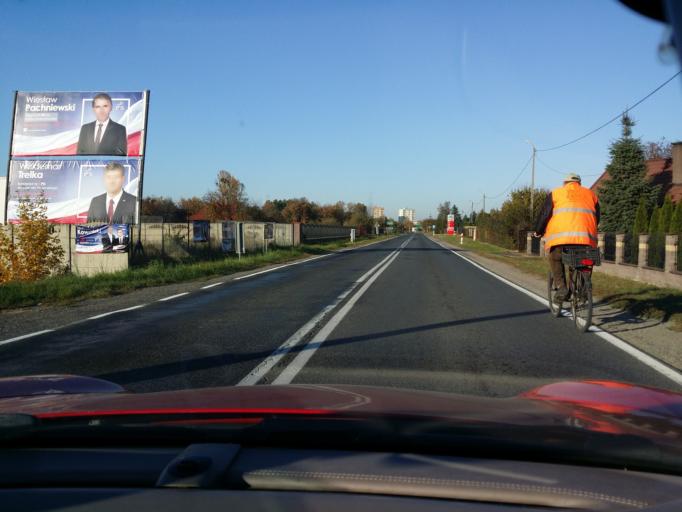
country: PL
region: Masovian Voivodeship
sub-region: Powiat radomski
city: Trablice
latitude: 51.3552
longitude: 21.1296
